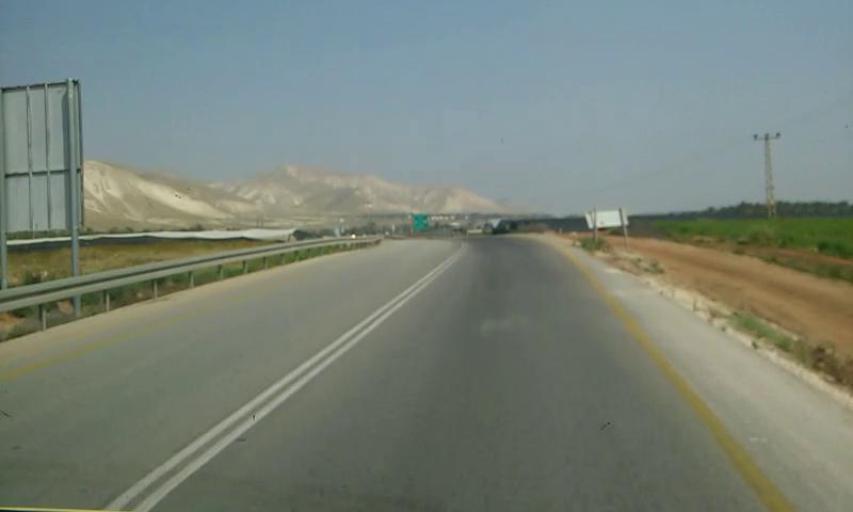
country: PS
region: West Bank
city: Al Fasayil
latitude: 32.0460
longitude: 35.4628
